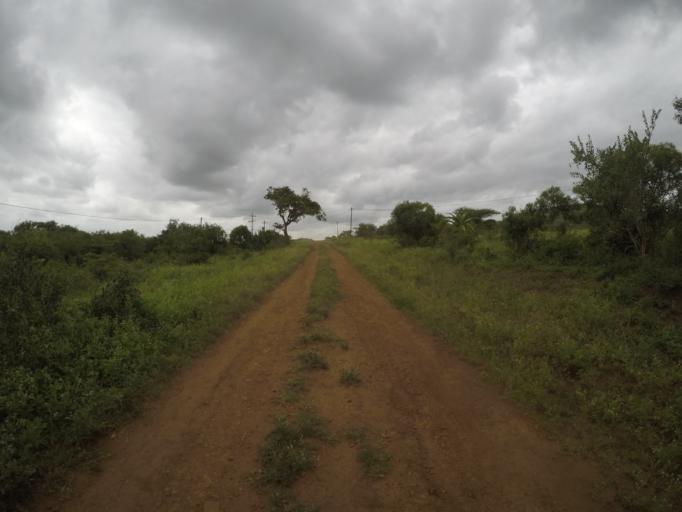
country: ZA
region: KwaZulu-Natal
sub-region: uThungulu District Municipality
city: Empangeni
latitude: -28.5866
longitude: 31.8630
